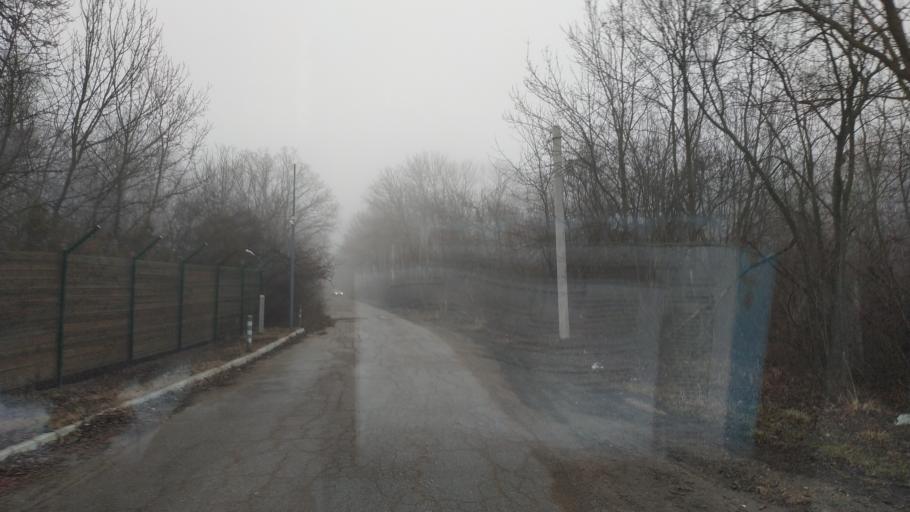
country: MD
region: Laloveni
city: Ialoveni
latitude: 46.9470
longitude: 28.7003
